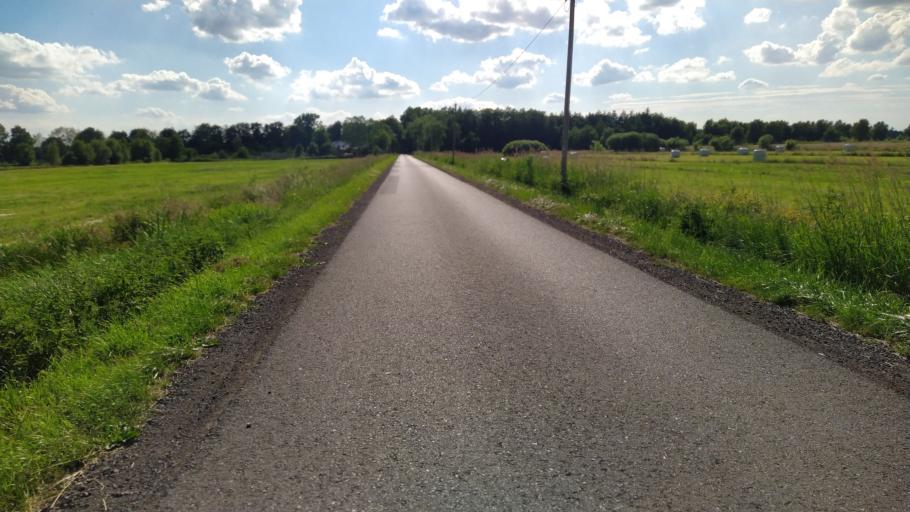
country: DE
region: Lower Saxony
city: Steinau
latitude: 53.6522
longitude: 8.9078
